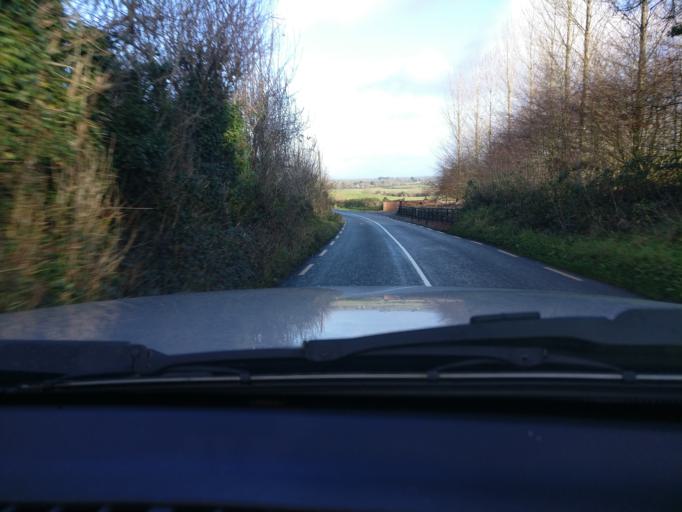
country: IE
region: Leinster
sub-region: An Iarmhi
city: Kilbeggan
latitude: 53.4642
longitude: -7.4958
